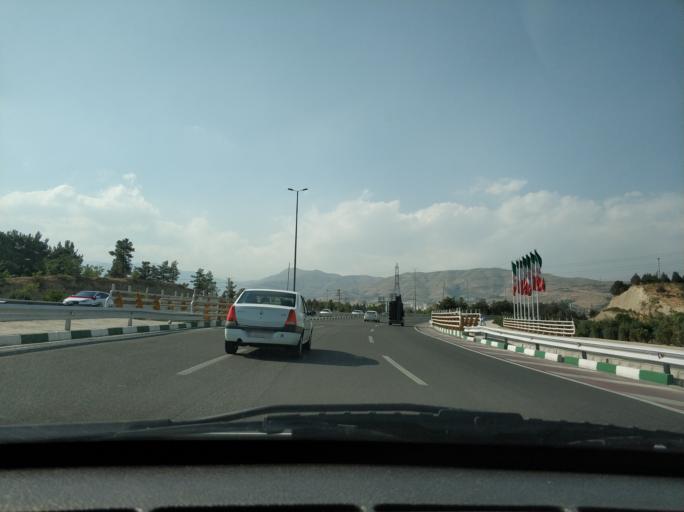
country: IR
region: Tehran
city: Tajrish
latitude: 35.7689
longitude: 51.5352
